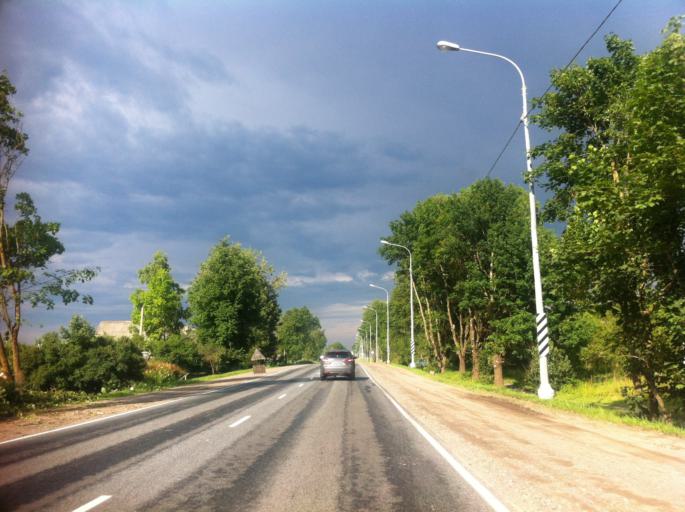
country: RU
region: Pskov
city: Plyussa
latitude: 58.2200
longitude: 29.3434
